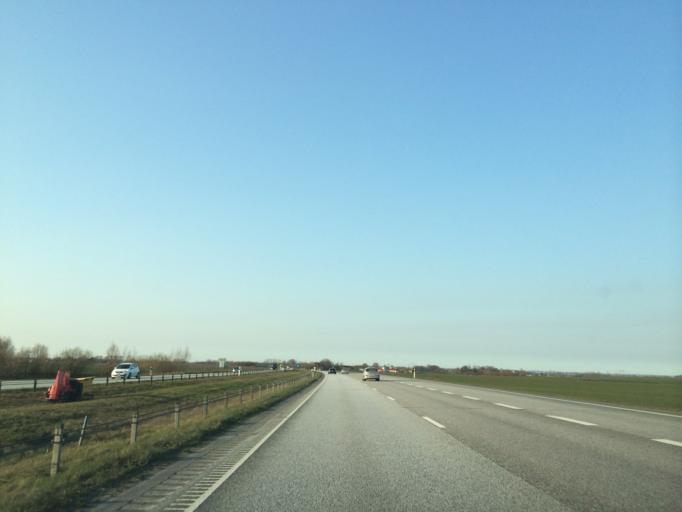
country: SE
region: Skane
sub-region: Burlovs Kommun
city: Arloev
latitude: 55.5926
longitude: 13.1168
